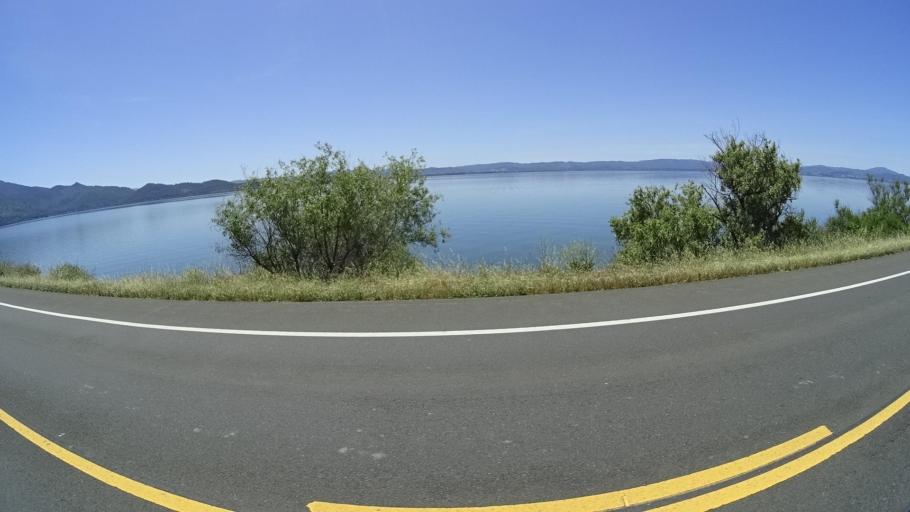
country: US
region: California
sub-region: Lake County
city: Lucerne
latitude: 39.0526
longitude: -122.7810
